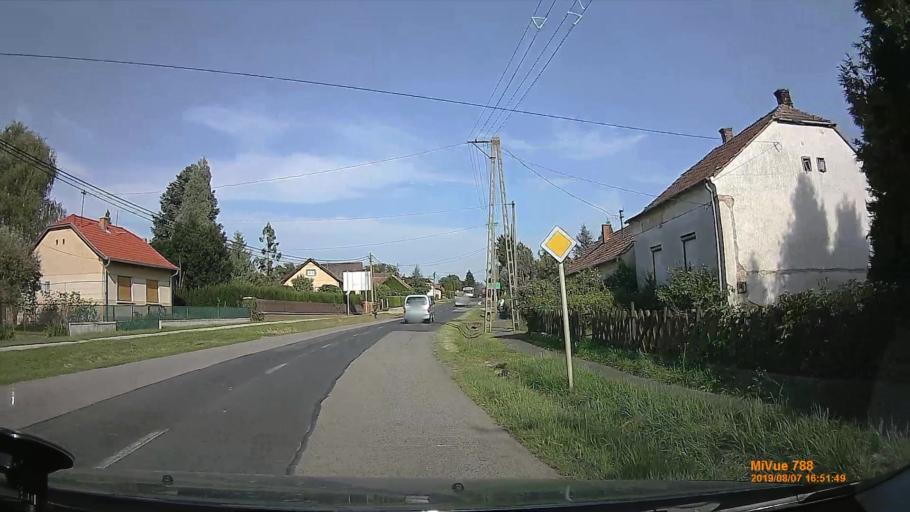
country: HU
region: Zala
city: Lenti
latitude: 46.6863
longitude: 16.6840
